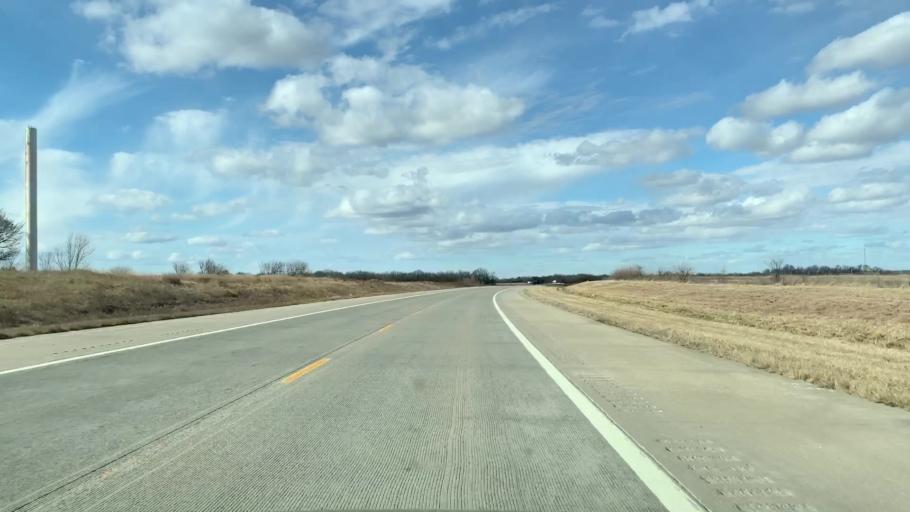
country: US
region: Kansas
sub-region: Labette County
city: Parsons
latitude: 37.3534
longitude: -95.2107
